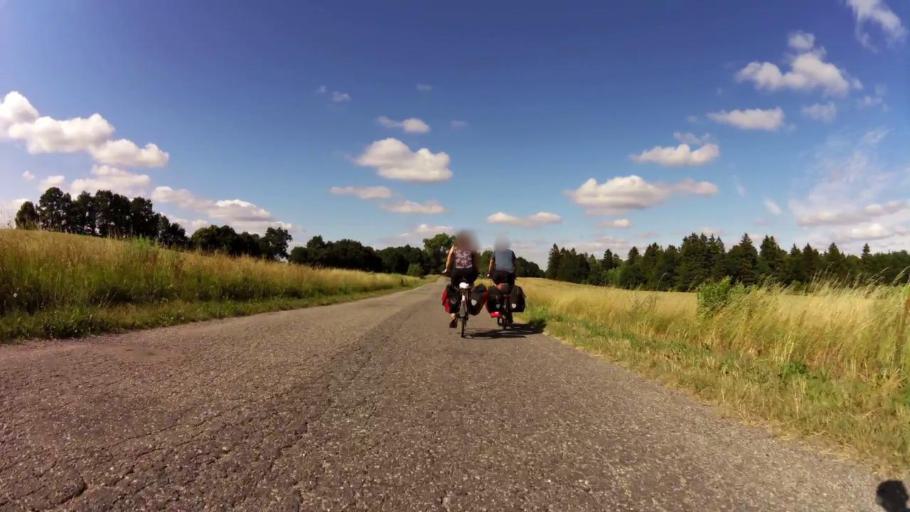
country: PL
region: West Pomeranian Voivodeship
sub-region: Powiat lobeski
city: Lobez
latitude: 53.6499
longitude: 15.6746
